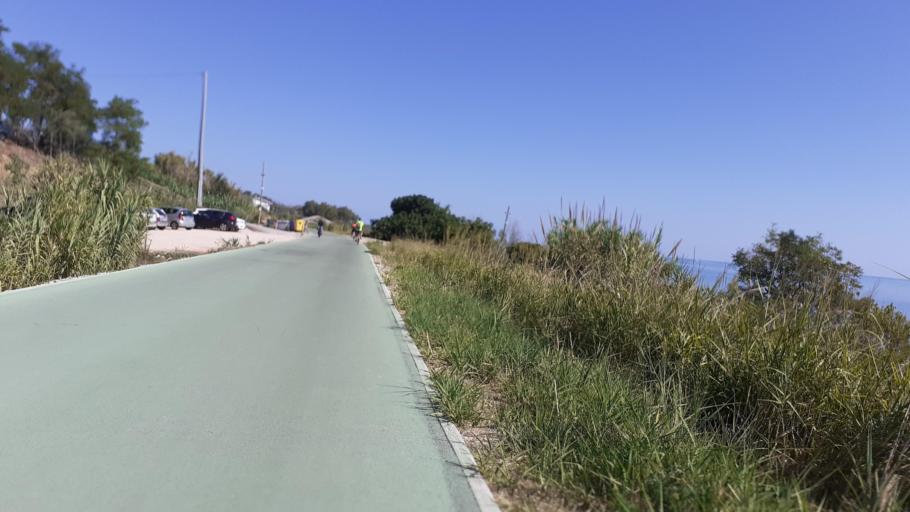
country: IT
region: Abruzzo
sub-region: Provincia di Chieti
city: Vasto
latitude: 42.1150
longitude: 14.7197
